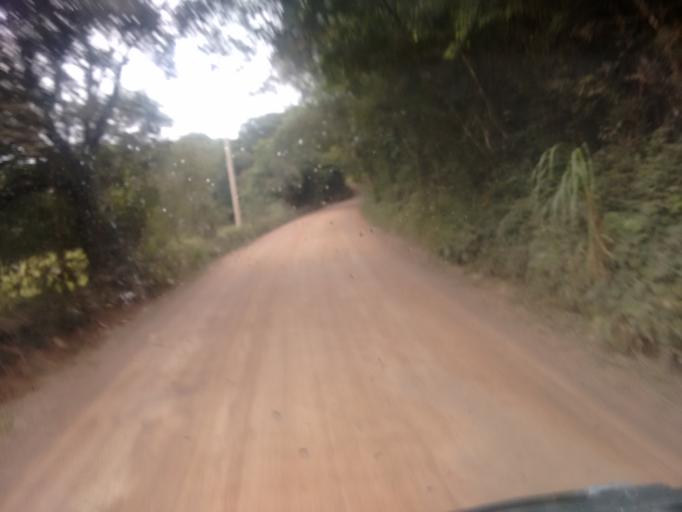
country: BR
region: Rio Grande do Sul
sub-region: Camaqua
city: Camaqua
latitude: -30.7294
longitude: -51.8424
